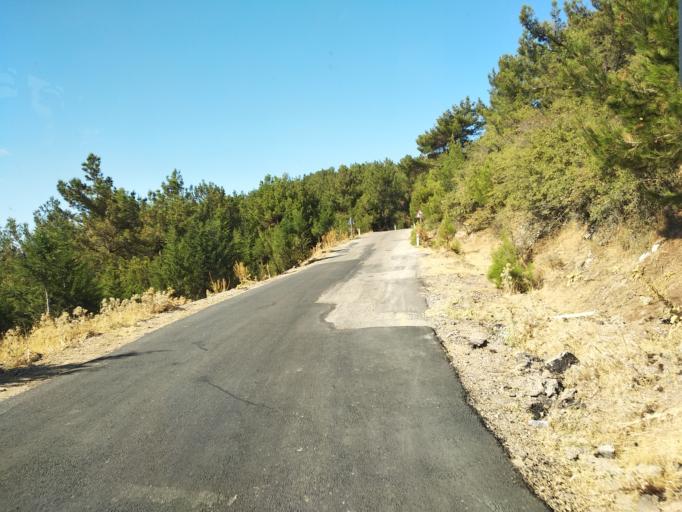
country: TR
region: Izmir
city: Gaziemir
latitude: 38.3072
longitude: 26.9984
